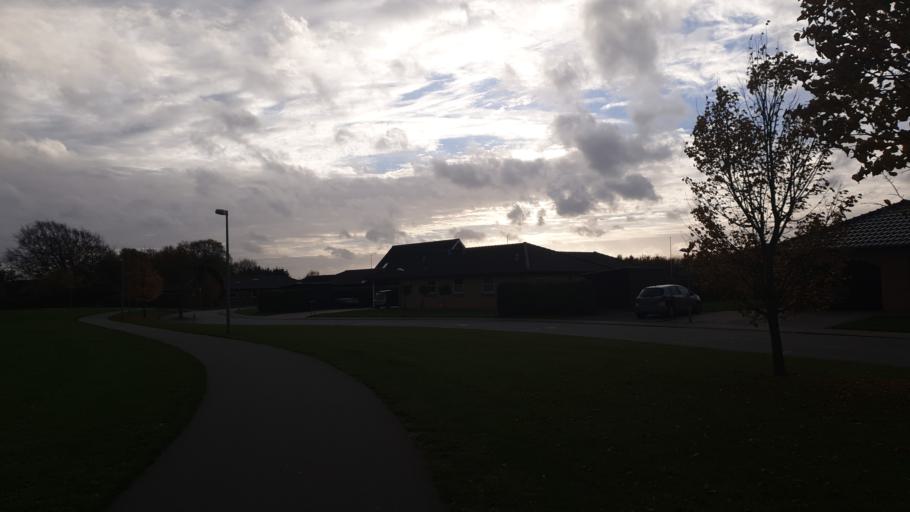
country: DK
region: Central Jutland
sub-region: Hedensted Kommune
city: Hedensted
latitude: 55.7919
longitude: 9.6938
